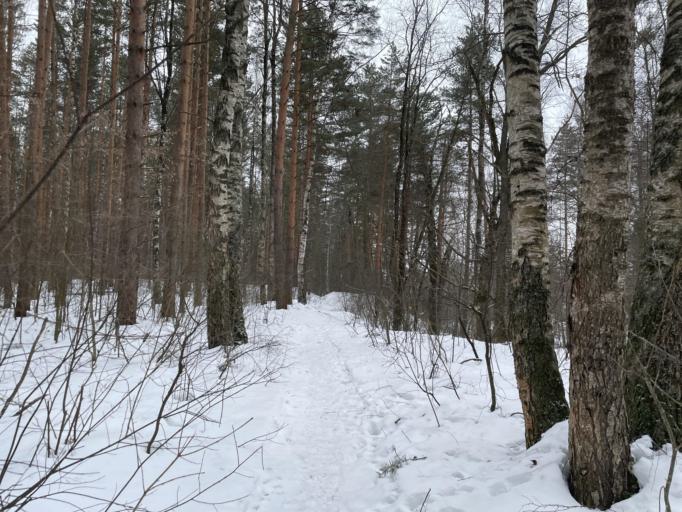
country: RU
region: Vladimir
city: Pokrov
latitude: 55.9399
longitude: 39.2371
